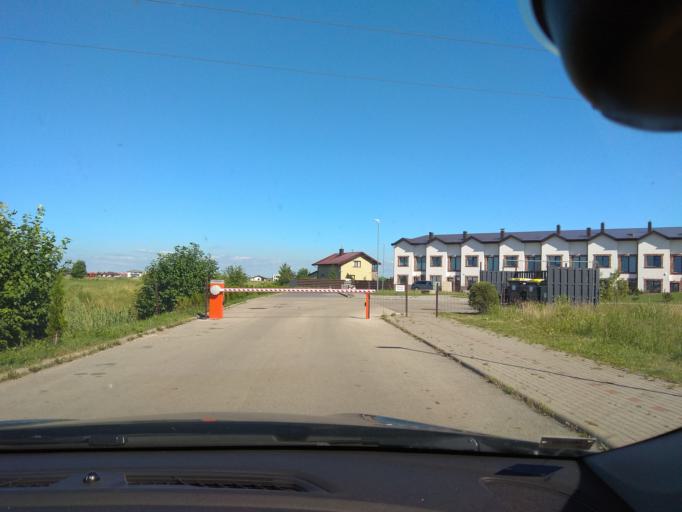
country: LT
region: Klaipedos apskritis
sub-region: Klaipeda
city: Klaipeda
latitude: 55.7490
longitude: 21.1819
